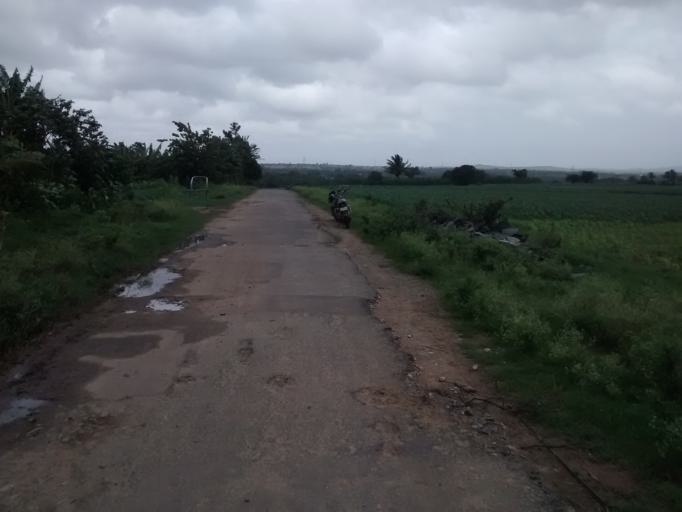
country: IN
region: Karnataka
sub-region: Hassan
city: Hassan
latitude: 12.9467
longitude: 76.1398
